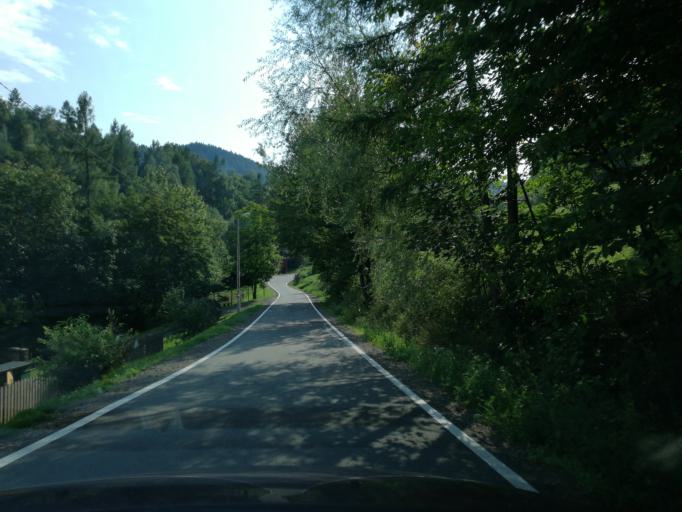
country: PL
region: Lesser Poland Voivodeship
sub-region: Powiat nowosadecki
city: Nawojowa
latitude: 49.5327
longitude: 20.7402
